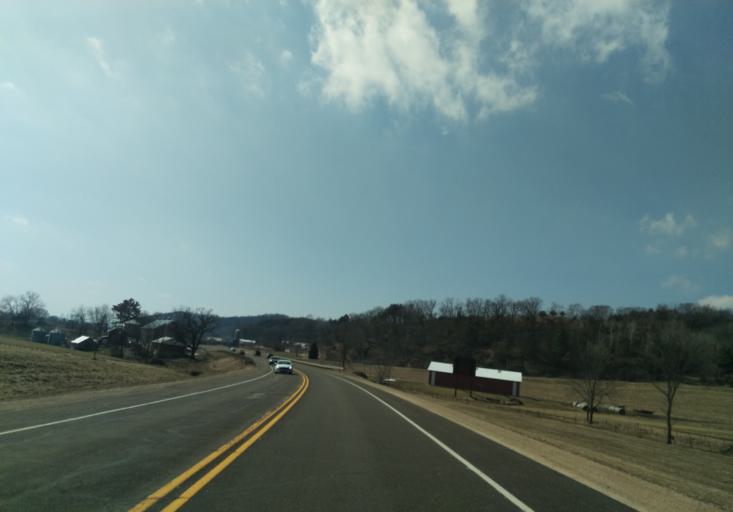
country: US
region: Wisconsin
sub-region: La Crosse County
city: La Crosse
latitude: 43.7655
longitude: -91.1756
